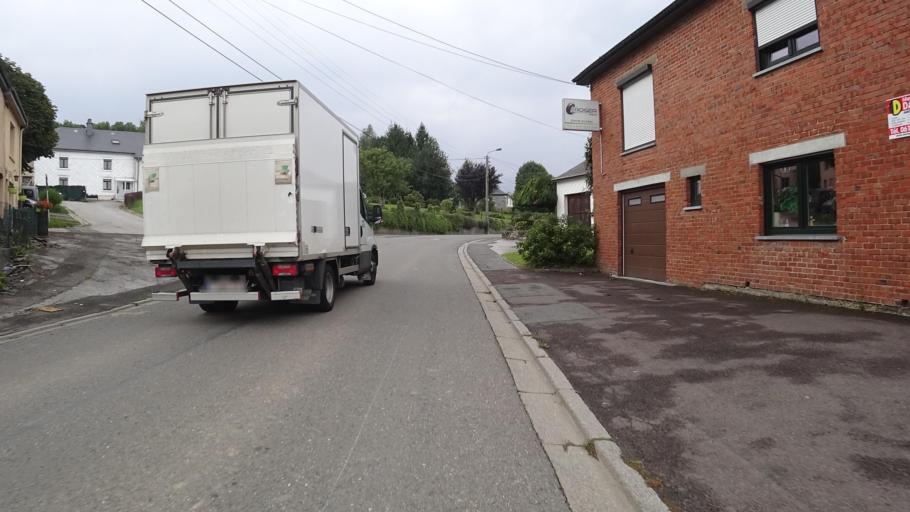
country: BE
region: Wallonia
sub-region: Province du Luxembourg
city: Chiny
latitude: 49.8130
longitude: 5.3276
